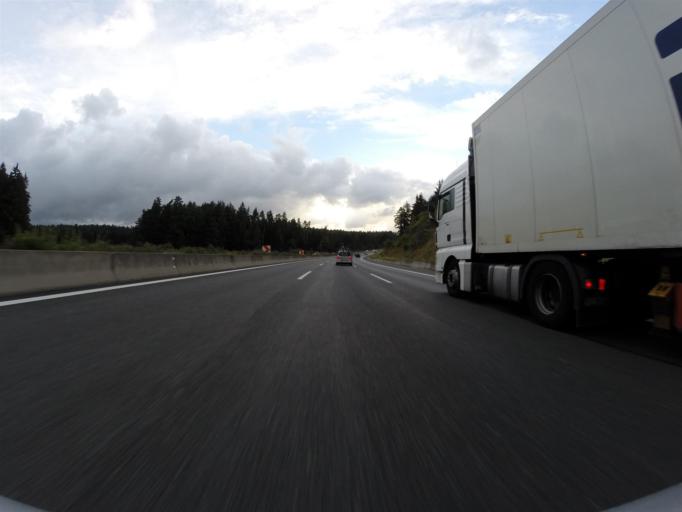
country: DE
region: Bavaria
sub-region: Upper Franconia
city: Pegnitz
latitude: 49.7196
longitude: 11.4810
